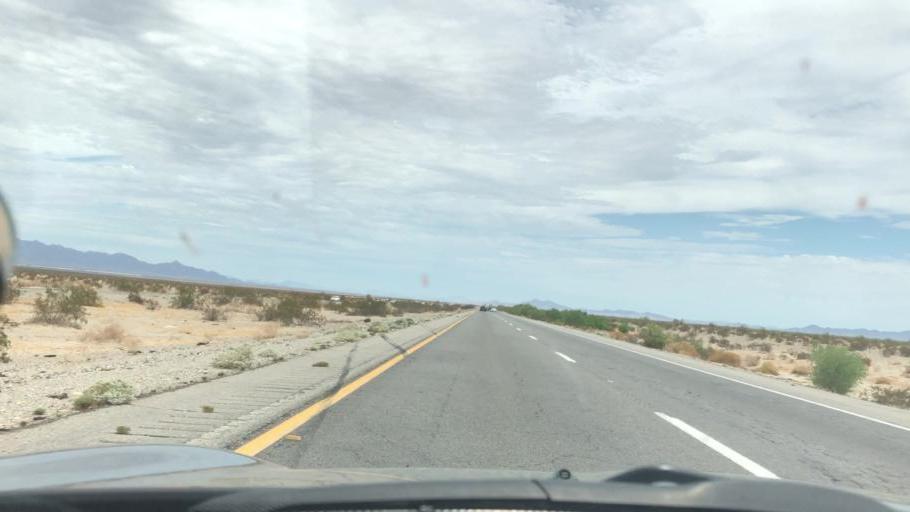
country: US
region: California
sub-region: Riverside County
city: Mesa Verde
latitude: 33.6483
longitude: -115.1288
